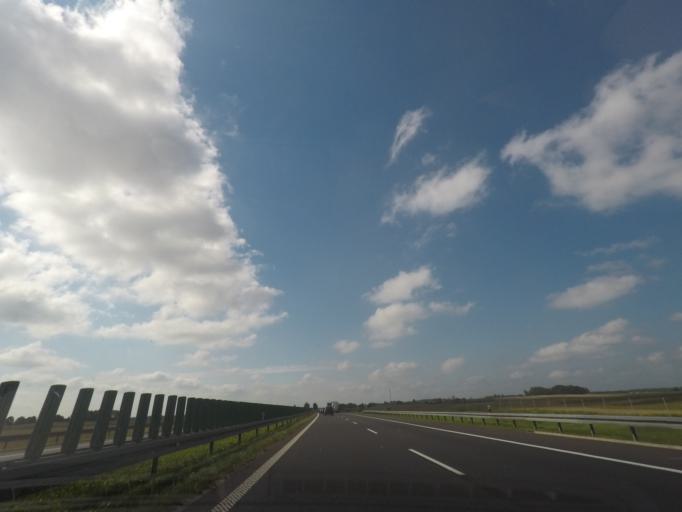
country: PL
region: Pomeranian Voivodeship
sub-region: Powiat starogardzki
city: Smetowo Graniczne
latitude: 53.7029
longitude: 18.6277
